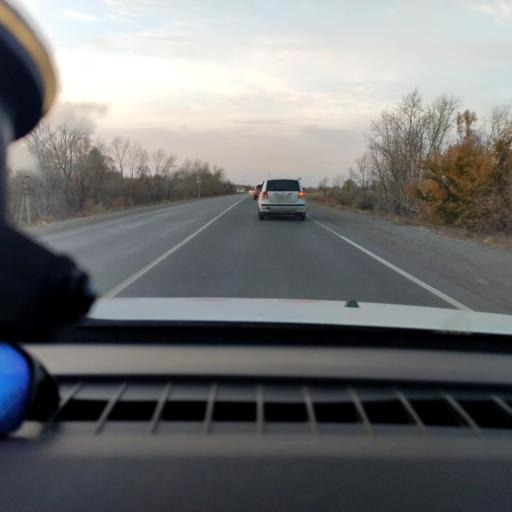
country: RU
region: Samara
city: Samara
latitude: 53.1036
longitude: 50.1381
